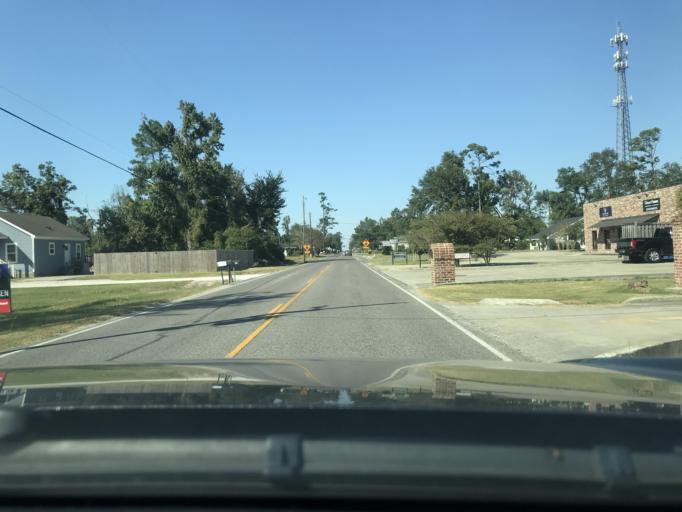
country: US
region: Louisiana
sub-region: Calcasieu Parish
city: Moss Bluff
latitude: 30.3092
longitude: -93.2001
